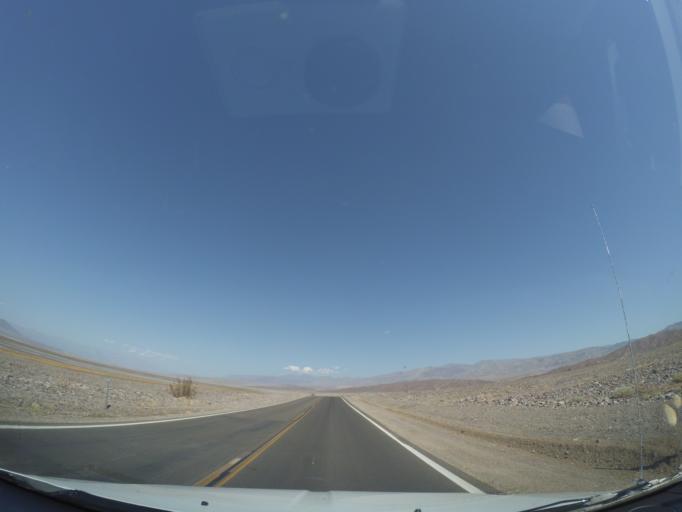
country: US
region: Nevada
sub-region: Nye County
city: Beatty
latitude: 36.5335
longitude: -116.8831
